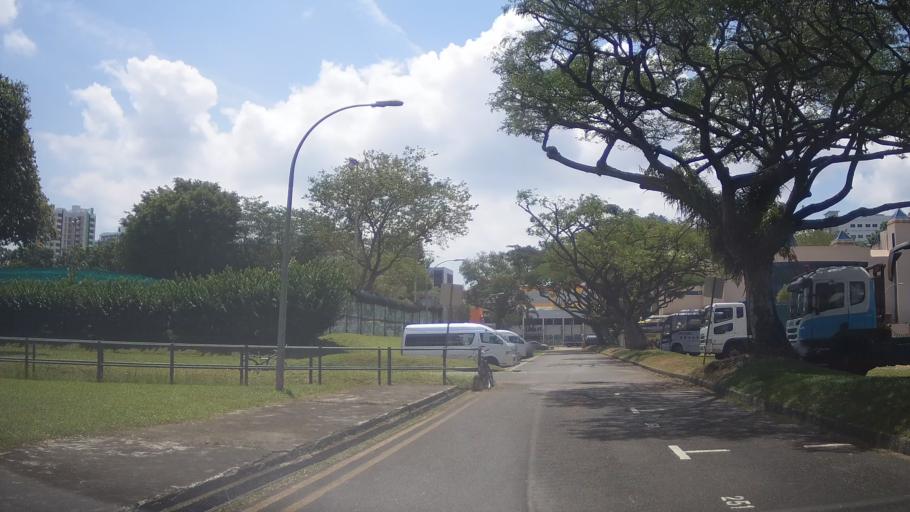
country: SG
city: Singapore
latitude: 1.3325
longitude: 103.7190
